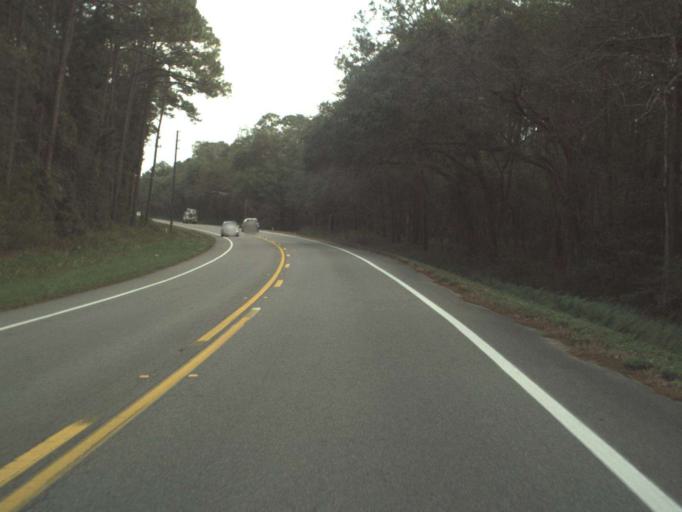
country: US
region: Florida
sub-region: Wakulla County
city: Crawfordville
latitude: 30.0762
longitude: -84.4076
